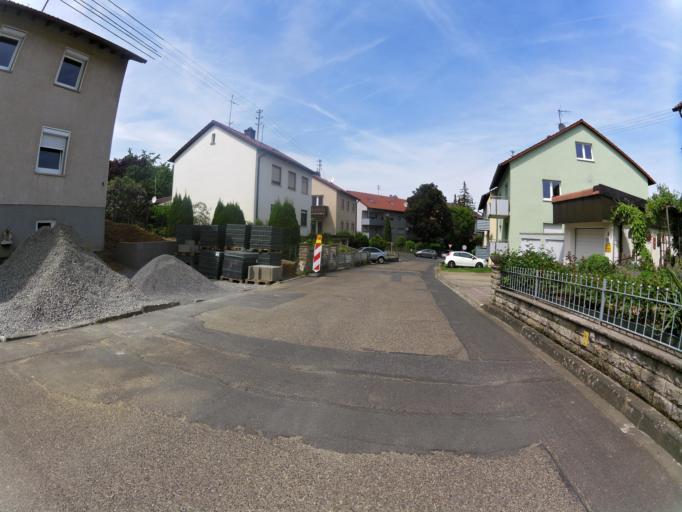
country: DE
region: Bavaria
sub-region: Regierungsbezirk Unterfranken
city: Ochsenfurt
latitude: 49.6677
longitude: 10.0420
